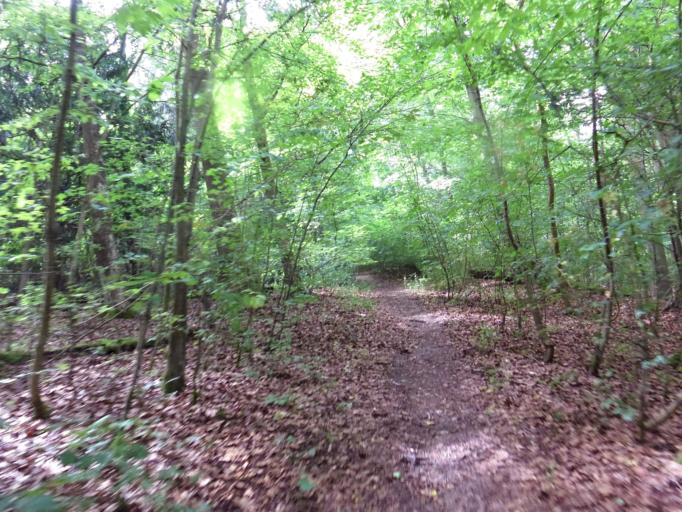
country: DE
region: Bavaria
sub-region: Regierungsbezirk Unterfranken
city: Wuerzburg
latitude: 49.7664
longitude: 9.9114
